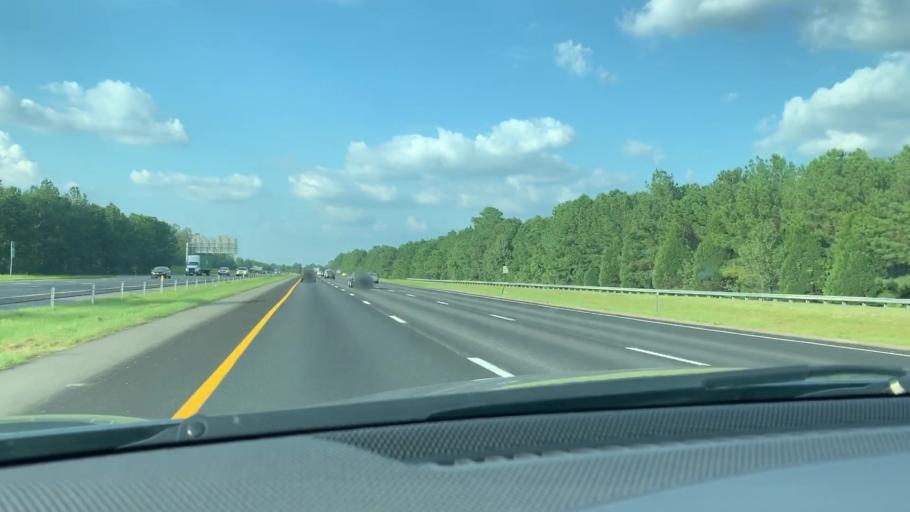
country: US
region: South Carolina
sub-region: Richland County
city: Forest Acres
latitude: 33.9795
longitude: -80.9542
